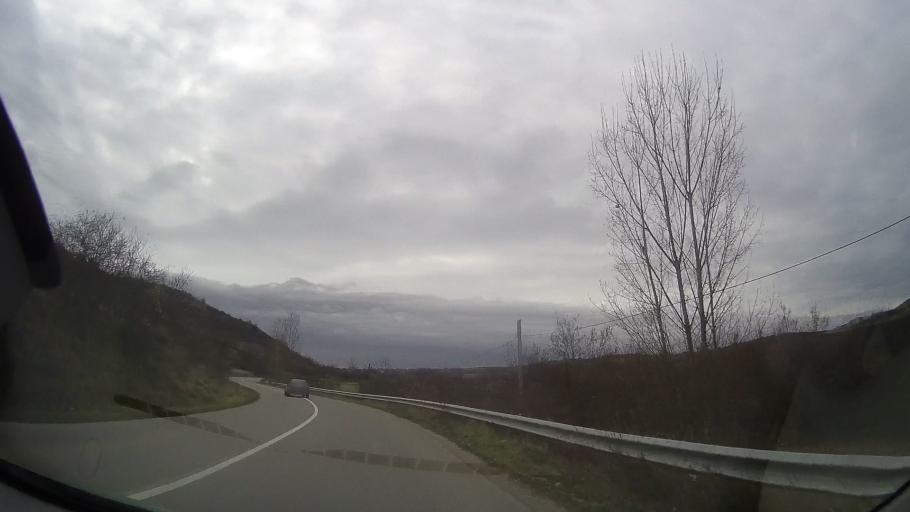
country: RO
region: Bistrita-Nasaud
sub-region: Comuna Milas
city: Milas
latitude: 46.8357
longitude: 24.4393
